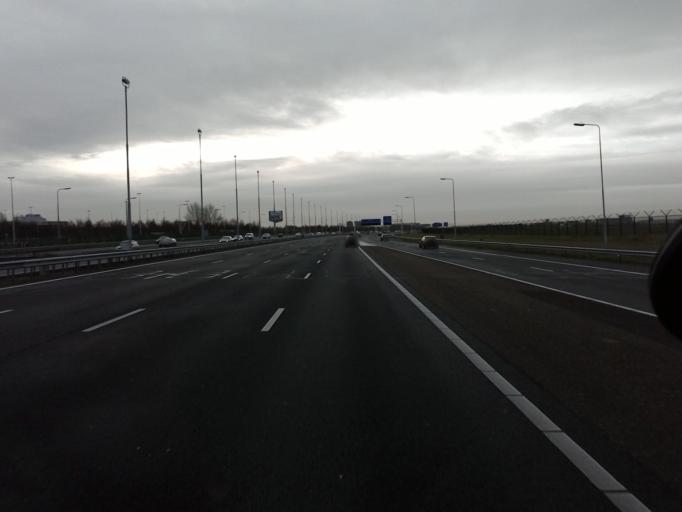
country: NL
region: North Holland
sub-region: Gemeente Aalsmeer
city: Aalsmeer
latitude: 52.3018
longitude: 4.7437
